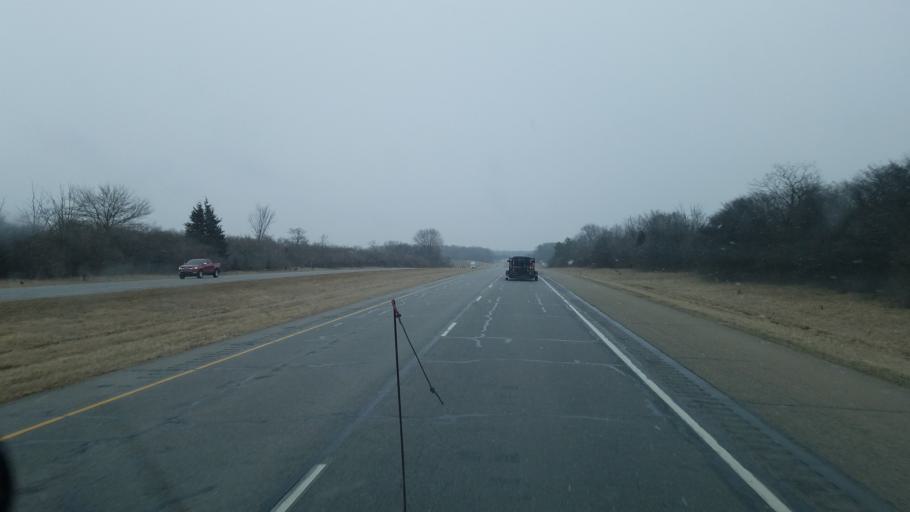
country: US
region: Indiana
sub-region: Miami County
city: Peru
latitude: 40.7961
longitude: -86.0355
